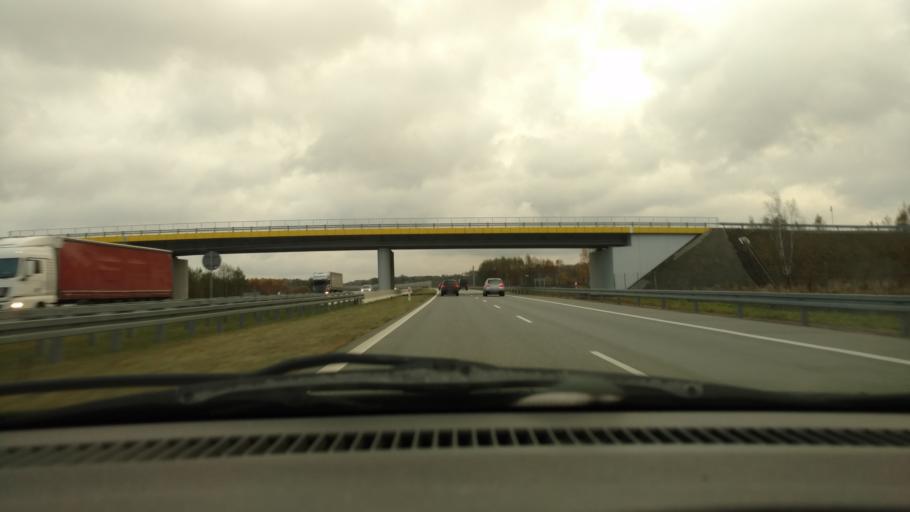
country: PL
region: Lodz Voivodeship
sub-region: Powiat lodzki wschodni
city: Rzgow
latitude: 51.6328
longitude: 19.4522
